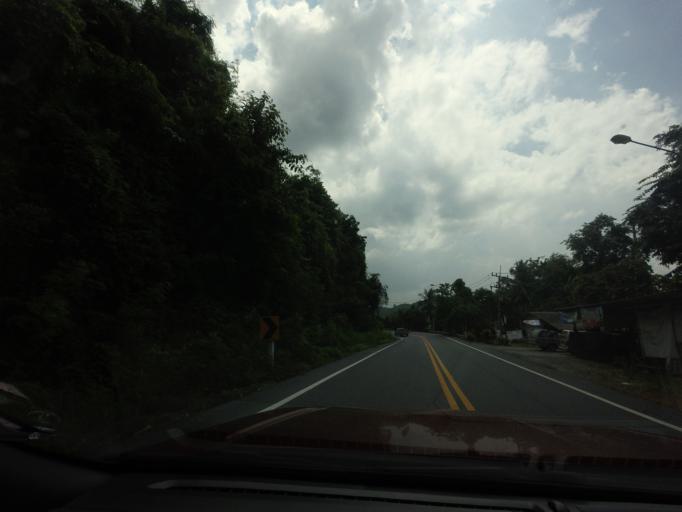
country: TH
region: Yala
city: Than To
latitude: 6.0398
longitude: 101.2091
